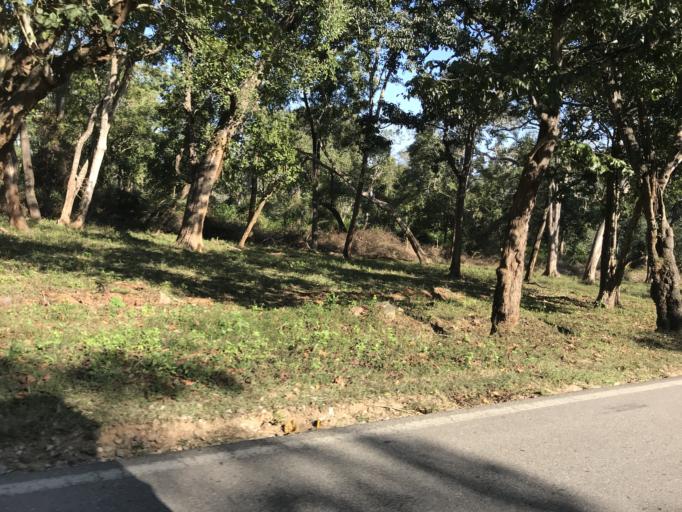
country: IN
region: Karnataka
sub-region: Mysore
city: Heggadadevankote
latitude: 11.9478
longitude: 76.2293
